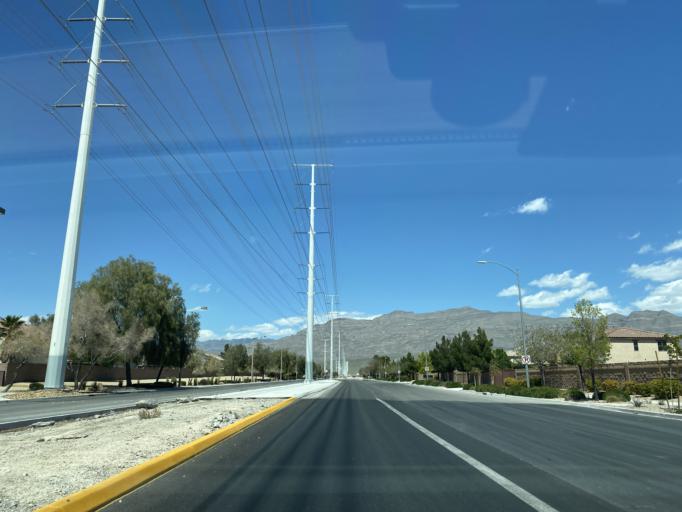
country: US
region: Nevada
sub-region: Clark County
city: North Las Vegas
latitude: 36.3076
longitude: -115.2071
